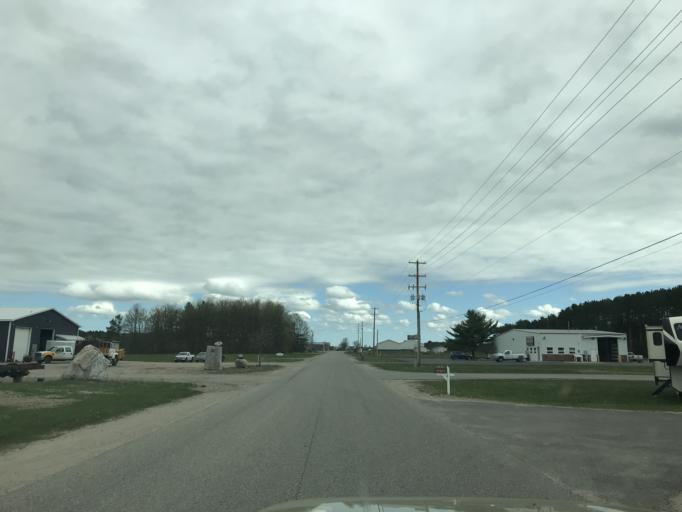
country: US
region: Michigan
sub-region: Otsego County
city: Gaylord
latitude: 45.0319
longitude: -84.6917
